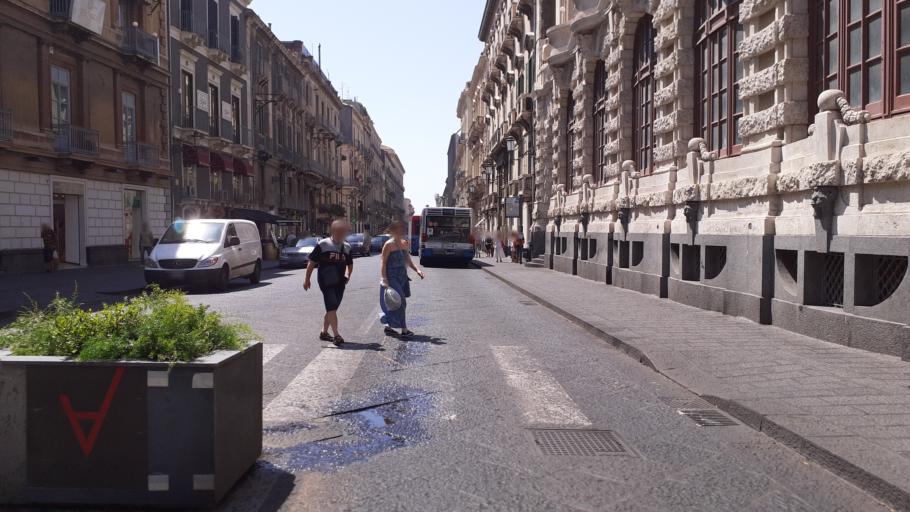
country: IT
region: Sicily
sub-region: Catania
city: Catania
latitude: 37.5103
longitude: 15.0855
